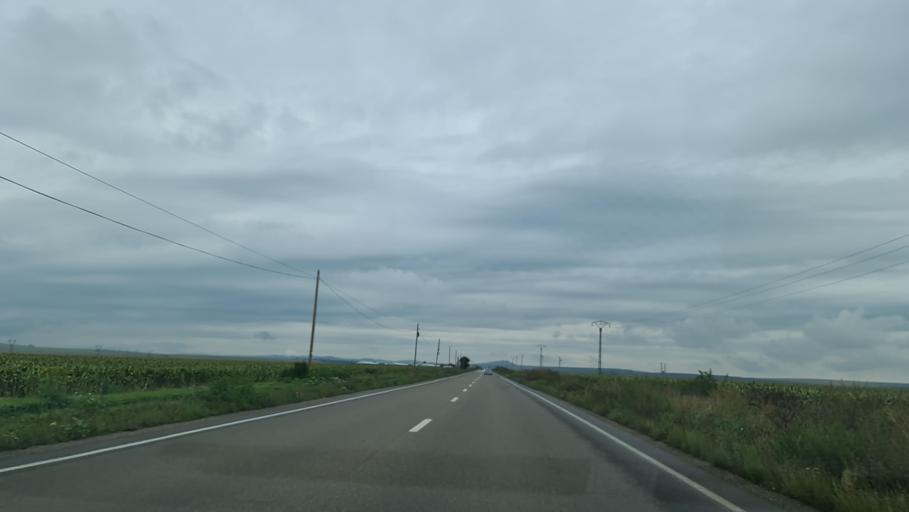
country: RO
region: Neamt
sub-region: Comuna Roznov
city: Slobozia
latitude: 46.8805
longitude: 26.5153
